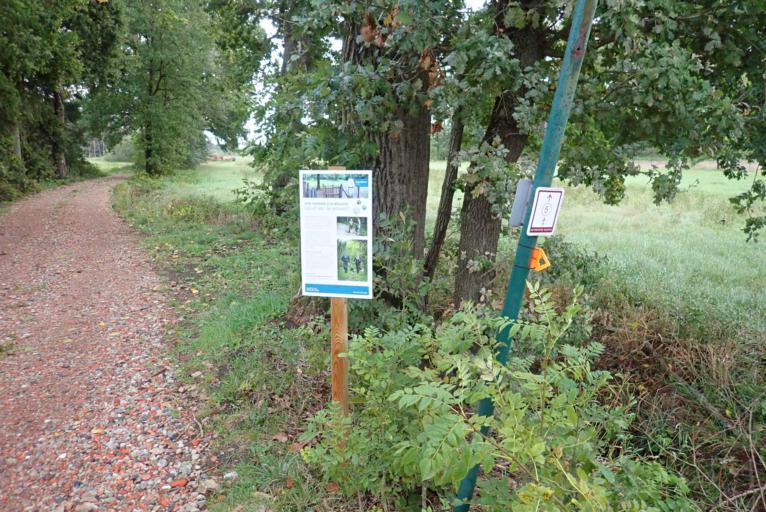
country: BE
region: Flanders
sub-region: Provincie Antwerpen
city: Hulshout
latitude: 51.0645
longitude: 4.7683
